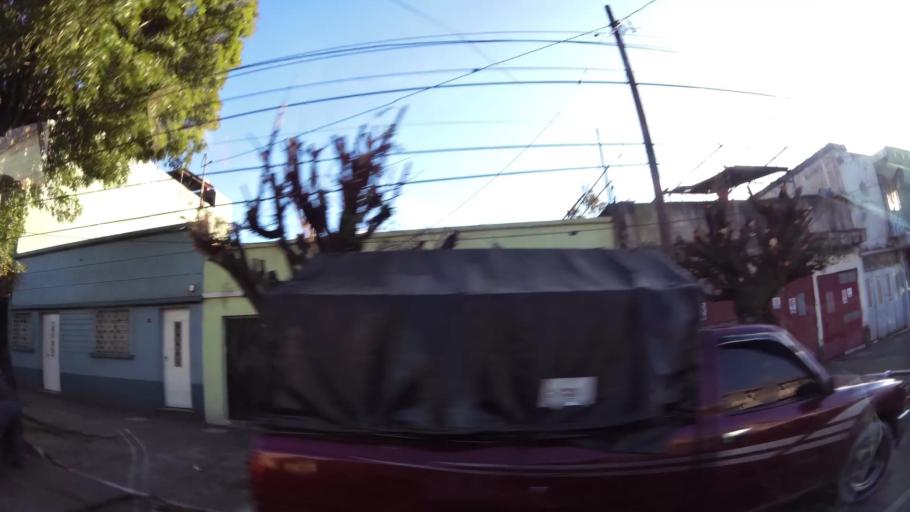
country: GT
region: Guatemala
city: Guatemala City
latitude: 14.6270
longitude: -90.5253
